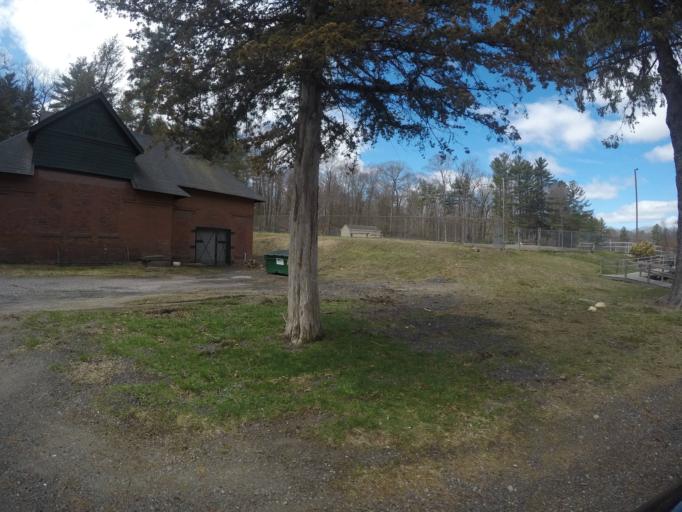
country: US
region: Massachusetts
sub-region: Bristol County
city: Easton
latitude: 42.0683
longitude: -71.1111
